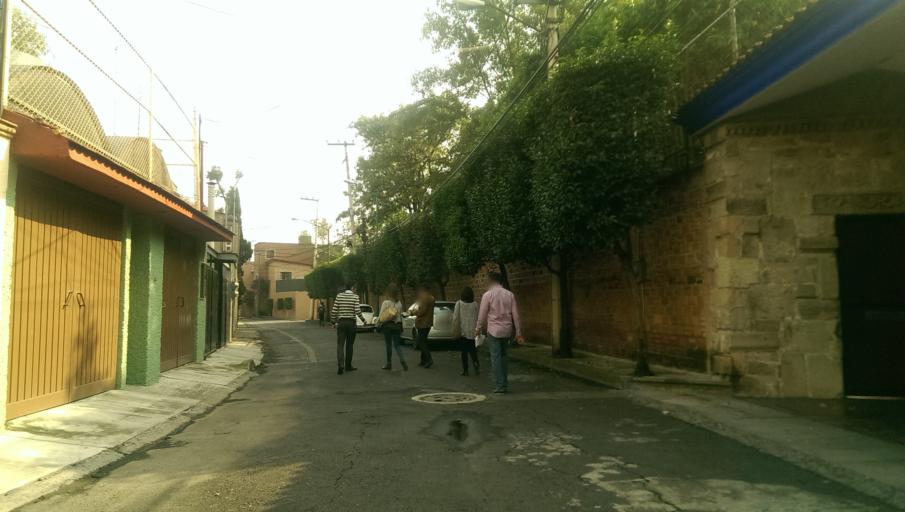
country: MX
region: Mexico City
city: Tlalpan
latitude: 19.2876
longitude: -99.1383
